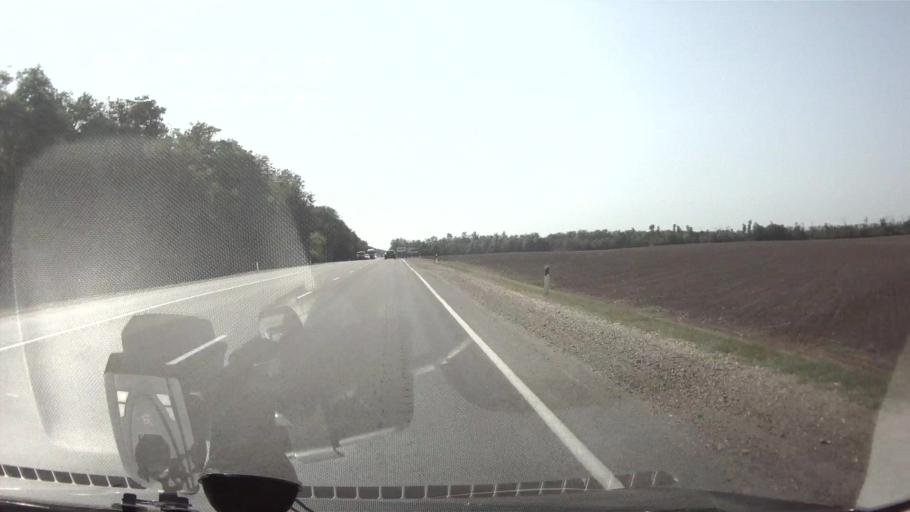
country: RU
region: Krasnodarskiy
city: Vasyurinskaya
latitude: 45.1476
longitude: 39.4353
